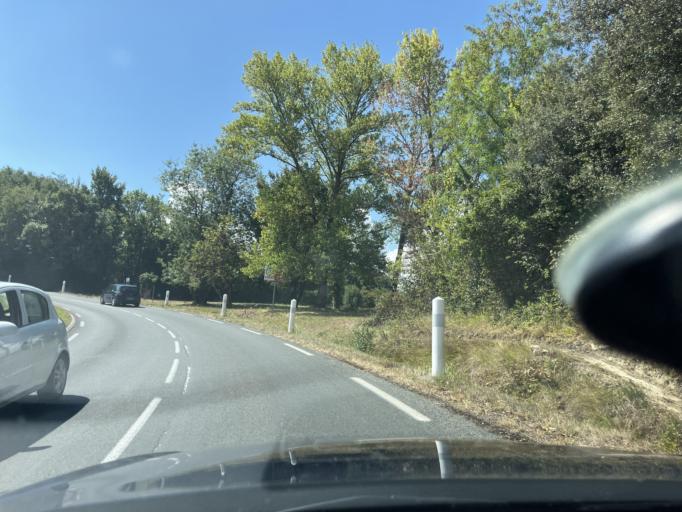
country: FR
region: Aquitaine
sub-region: Departement de la Gironde
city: Cantenac
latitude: 45.0745
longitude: -0.6320
